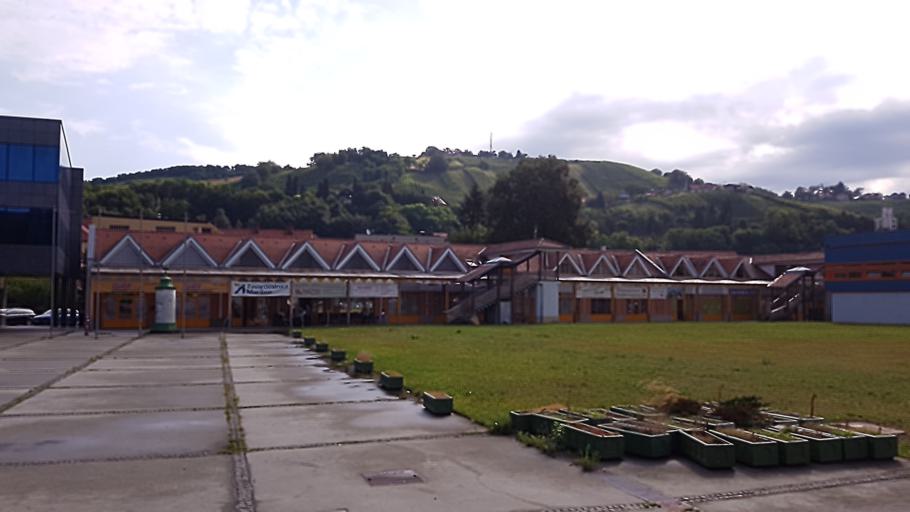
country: SI
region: Lendava-Lendva
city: Lendava
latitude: 46.5622
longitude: 16.4524
